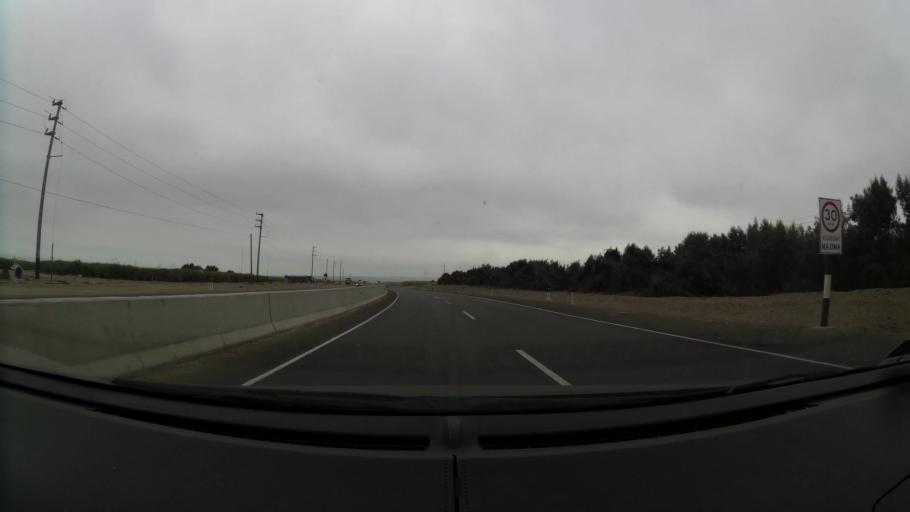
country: PE
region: La Libertad
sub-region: Provincia de Trujillo
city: Salaverry
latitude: -8.2960
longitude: -78.9087
